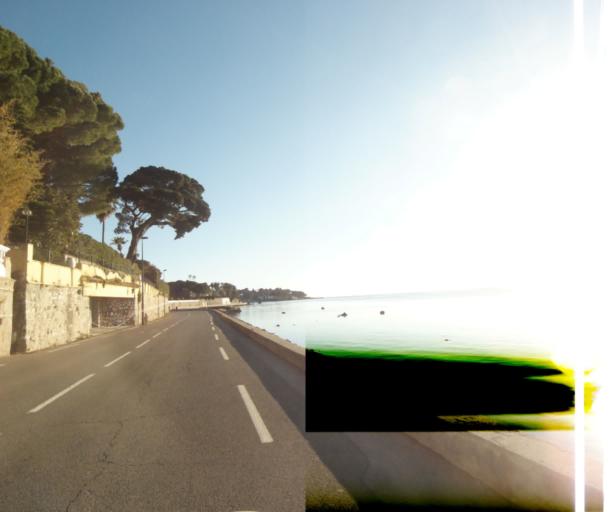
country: FR
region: Provence-Alpes-Cote d'Azur
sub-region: Departement des Alpes-Maritimes
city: Antibes
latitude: 43.5591
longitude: 7.1218
